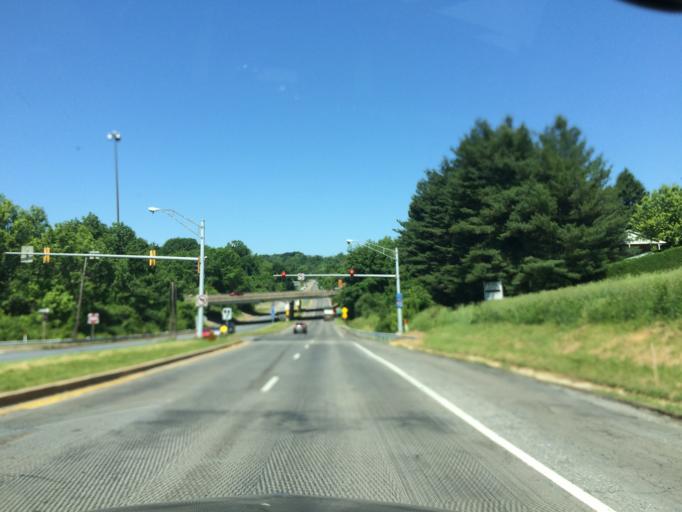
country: US
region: Maryland
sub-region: Frederick County
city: Braddock Heights
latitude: 39.4215
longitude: -77.4832
